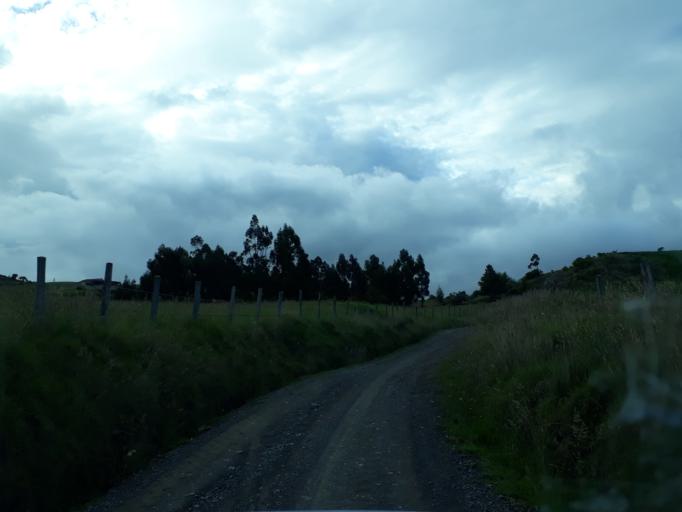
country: CO
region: Cundinamarca
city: Carmen de Carupa
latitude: 5.3122
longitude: -73.9101
